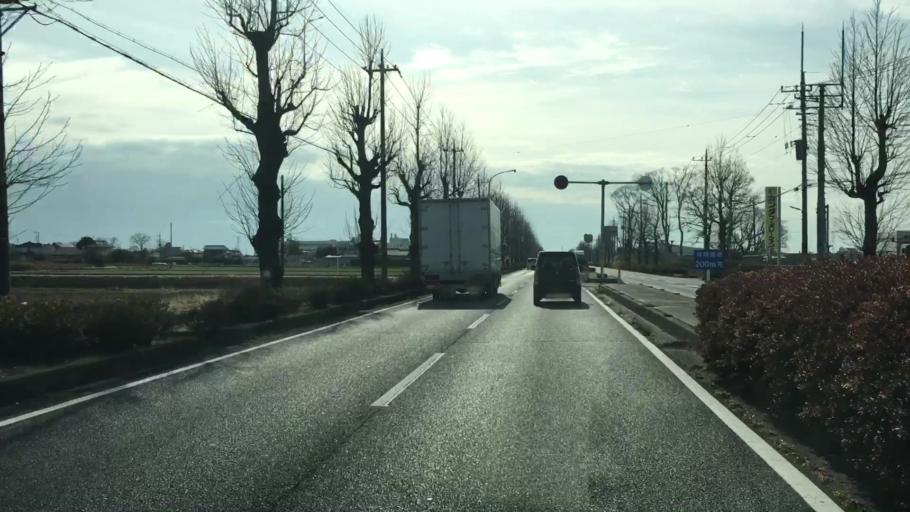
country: JP
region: Saitama
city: Menuma
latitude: 36.1962
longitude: 139.3704
